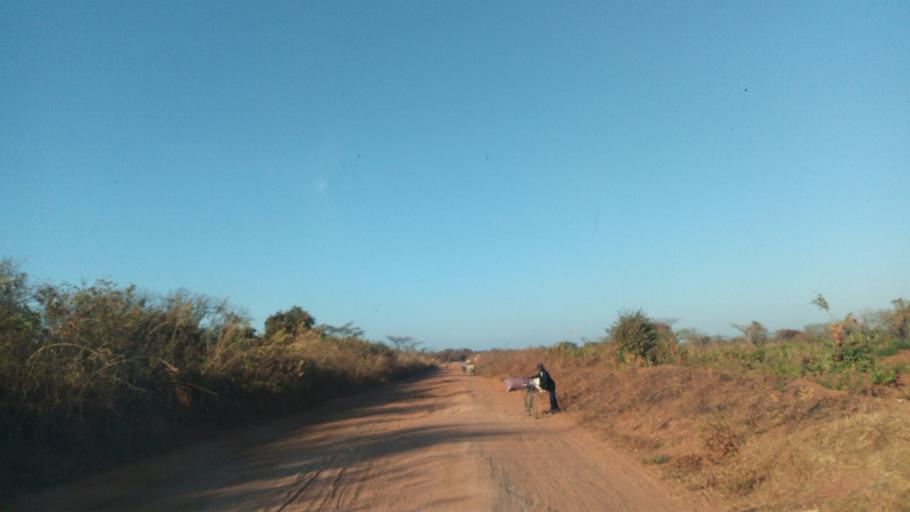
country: ZM
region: Luapula
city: Mwense
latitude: -10.4146
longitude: 28.6084
